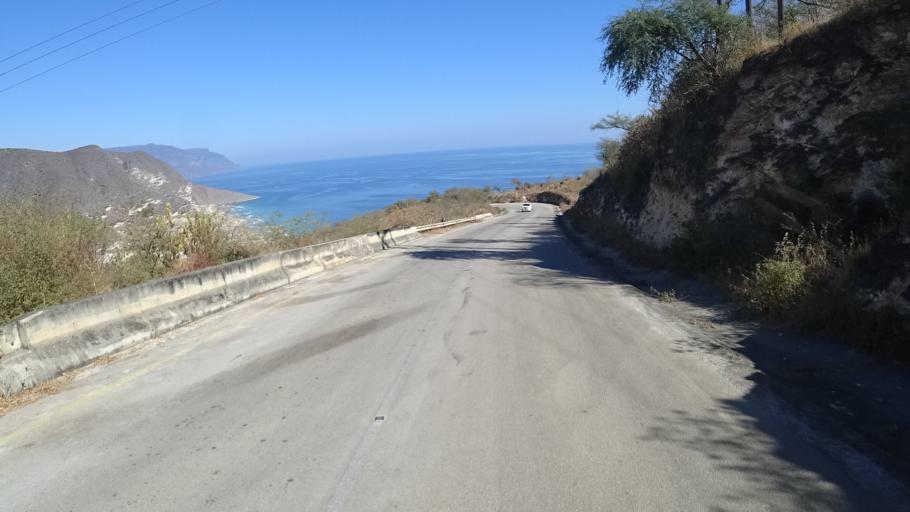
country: YE
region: Al Mahrah
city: Hawf
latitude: 16.7457
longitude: 53.4079
